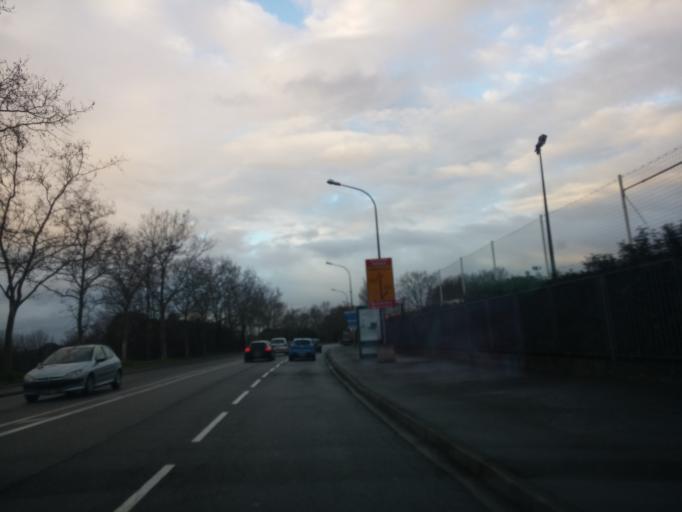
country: FR
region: Midi-Pyrenees
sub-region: Departement de la Haute-Garonne
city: Toulouse
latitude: 43.5789
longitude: 1.4369
